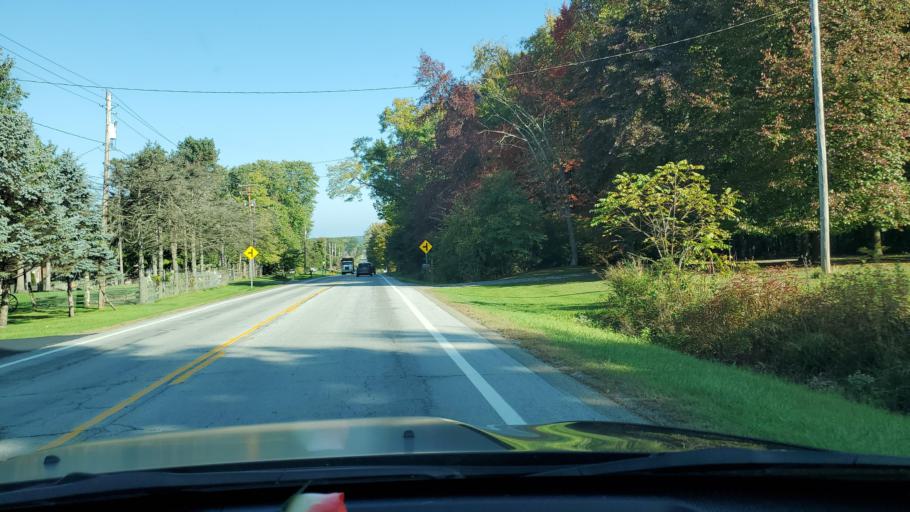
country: US
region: Ohio
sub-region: Trumbull County
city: Brookfield Center
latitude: 41.2426
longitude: -80.5681
